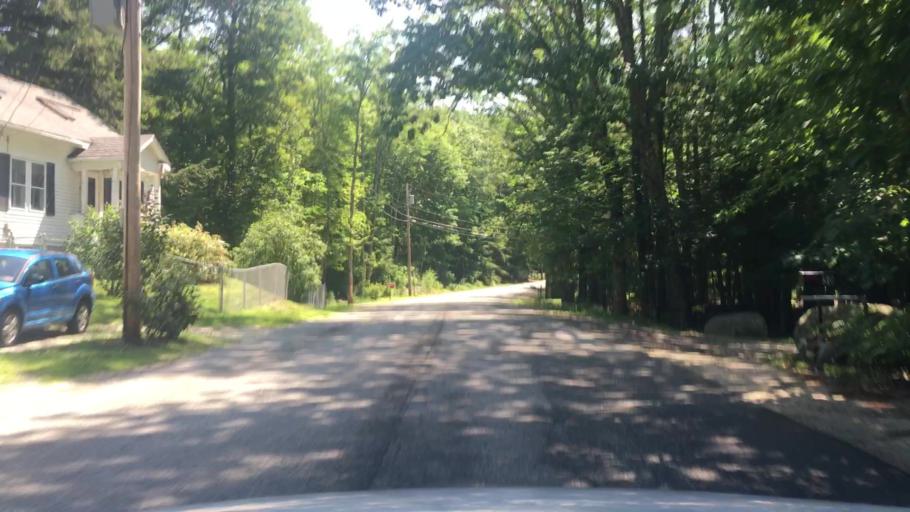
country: US
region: Maine
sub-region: Cumberland County
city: Cumberland Center
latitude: 43.8505
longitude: -70.3152
